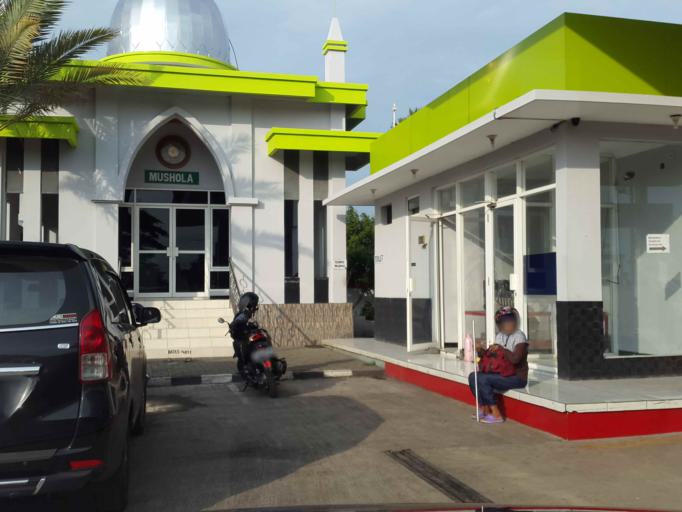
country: ID
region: Central Java
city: Dukuhturi
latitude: -6.9506
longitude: 109.0470
